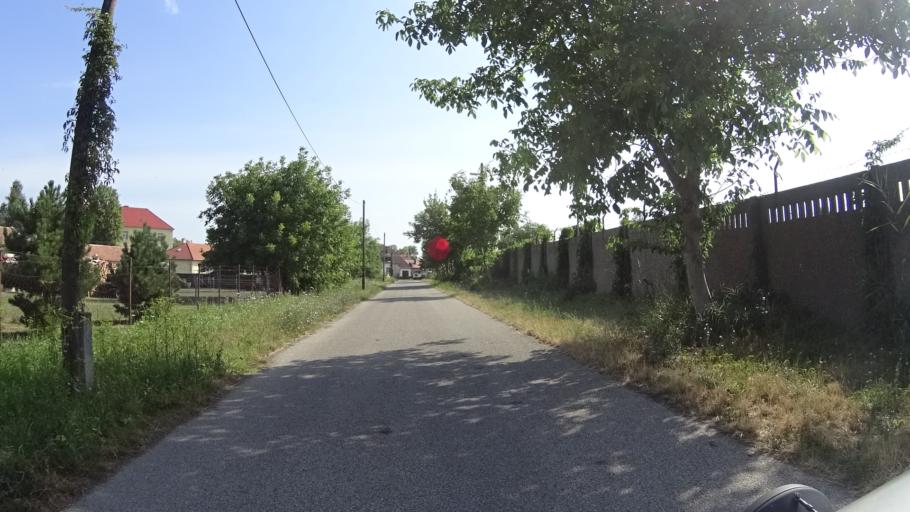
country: HU
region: Gyor-Moson-Sopron
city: Gyor
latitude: 47.6803
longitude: 17.6066
